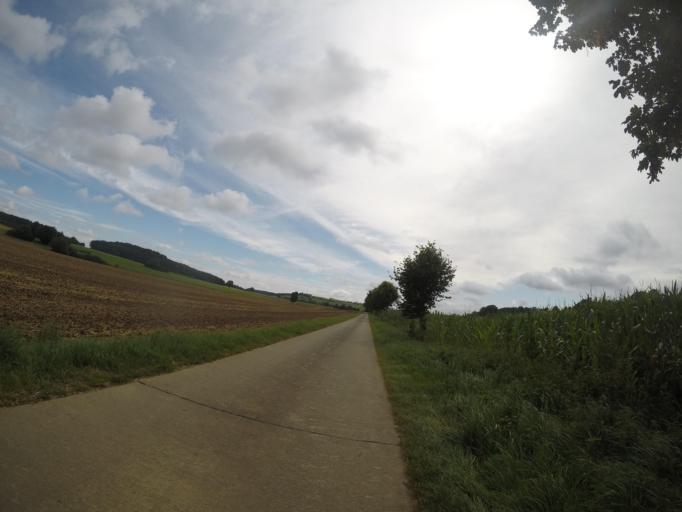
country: DE
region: Baden-Wuerttemberg
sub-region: Tuebingen Region
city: Laichingen
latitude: 48.4573
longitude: 9.6499
